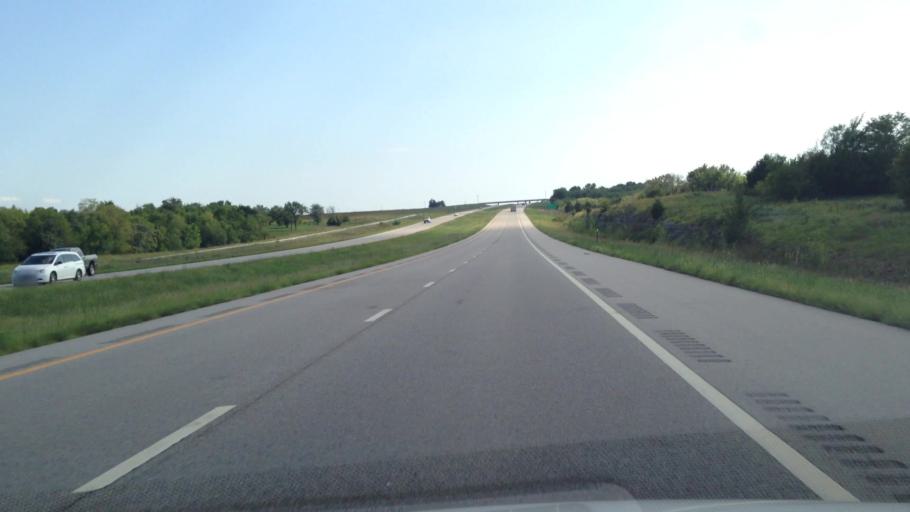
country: US
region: Kansas
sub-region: Linn County
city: La Cygne
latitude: 38.4157
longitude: -94.6879
